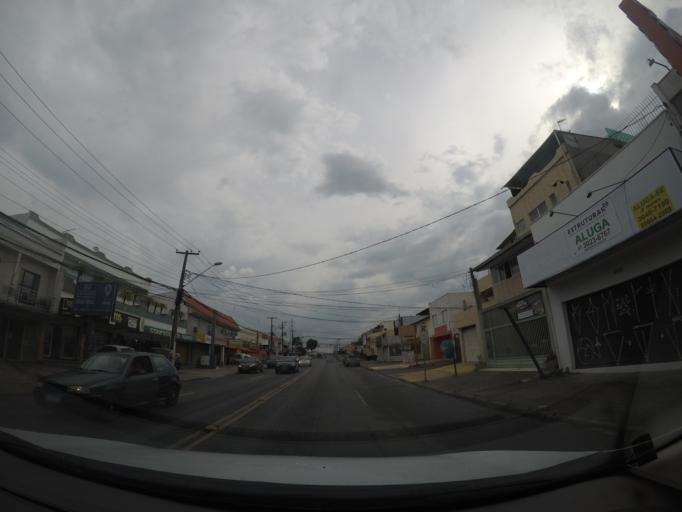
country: BR
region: Parana
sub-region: Sao Jose Dos Pinhais
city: Sao Jose dos Pinhais
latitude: -25.5318
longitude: -49.2599
